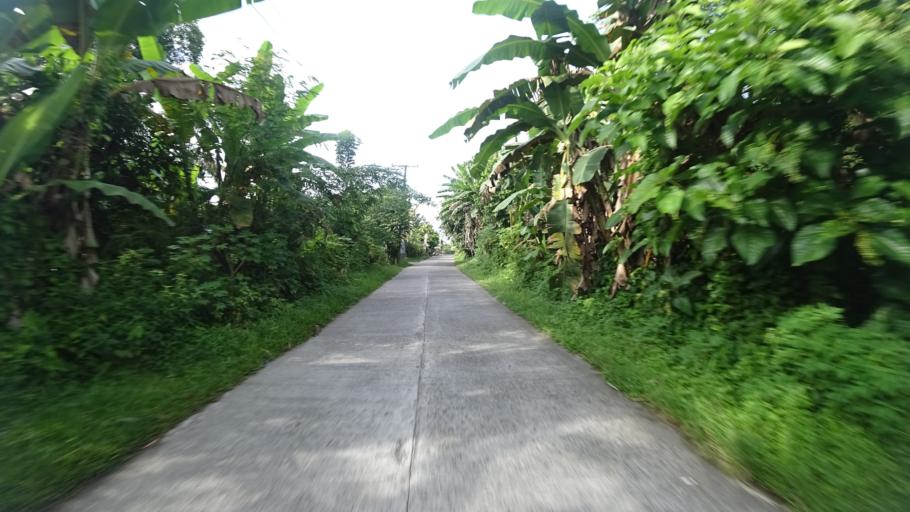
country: PH
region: Eastern Visayas
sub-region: Province of Leyte
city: Alangalang
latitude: 11.1750
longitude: 124.8717
